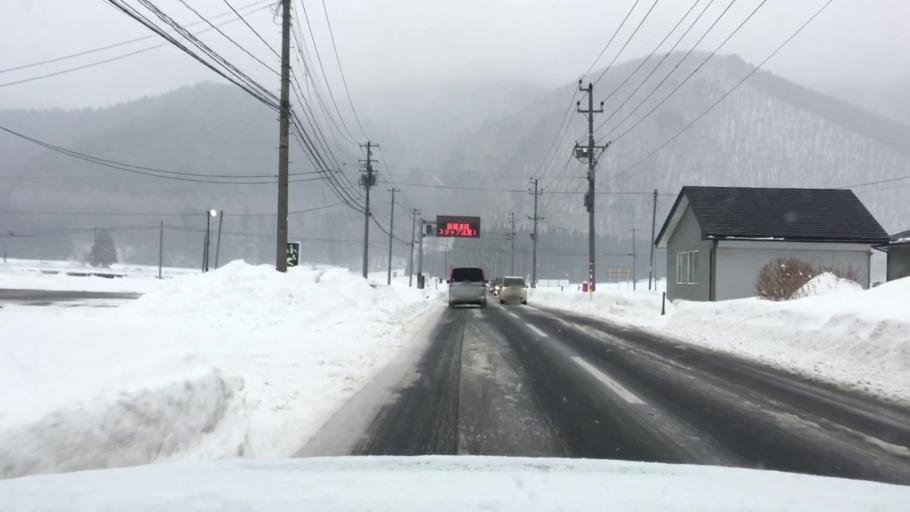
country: JP
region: Akita
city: Hanawa
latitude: 40.0782
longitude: 141.0222
